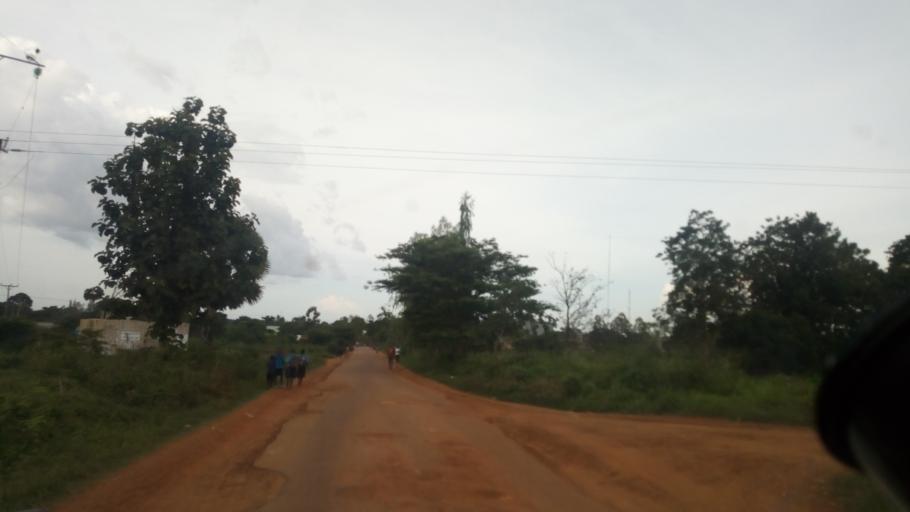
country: UG
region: Northern Region
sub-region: Lira District
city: Lira
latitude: 2.2630
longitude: 32.8628
